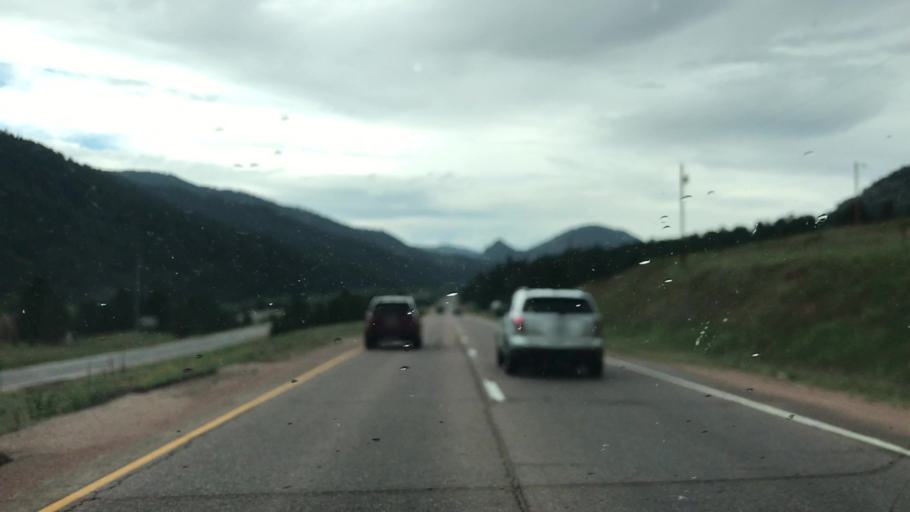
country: US
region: Colorado
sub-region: El Paso County
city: Cascade-Chipita Park
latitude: 38.9395
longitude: -105.0121
